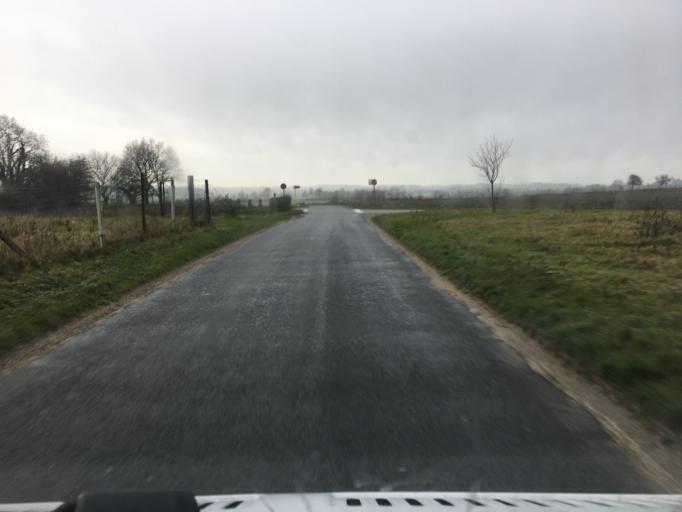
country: FR
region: Picardie
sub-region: Departement de la Somme
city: Saint-Valery-sur-Somme
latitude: 50.1778
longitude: 1.6220
